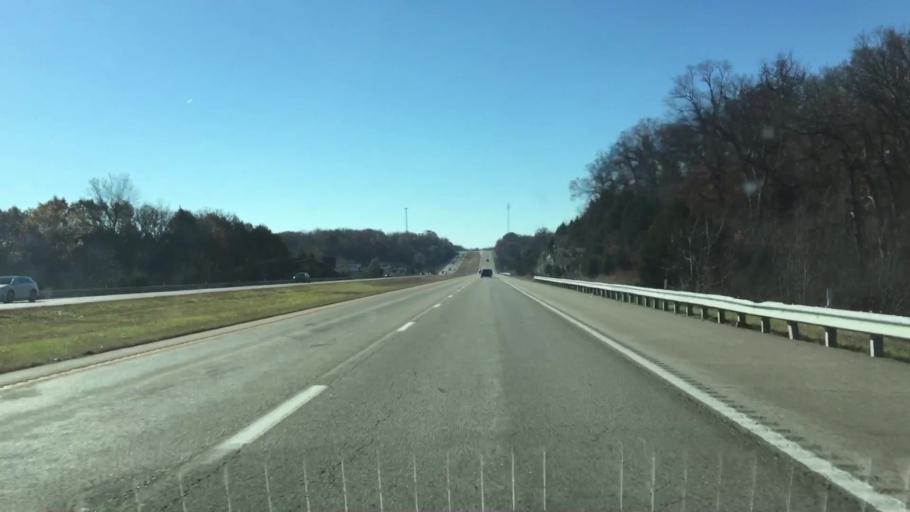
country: US
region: Missouri
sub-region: Cole County
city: Wardsville
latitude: 38.4946
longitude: -92.2691
